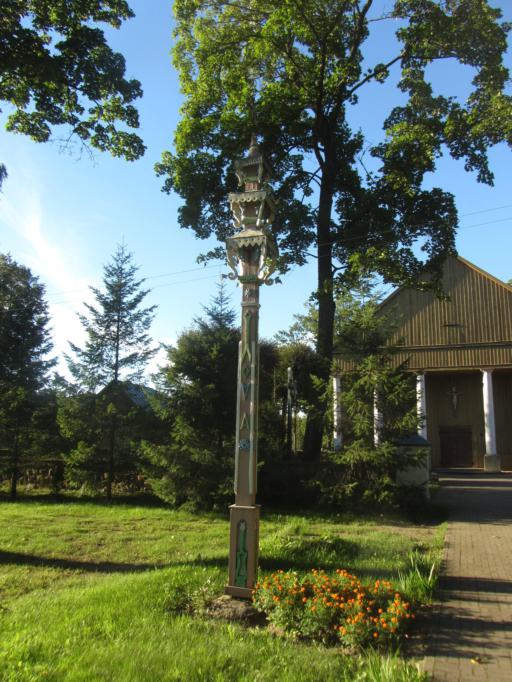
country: LT
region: Alytaus apskritis
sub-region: Alytus
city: Alytus
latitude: 54.4659
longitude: 24.0545
